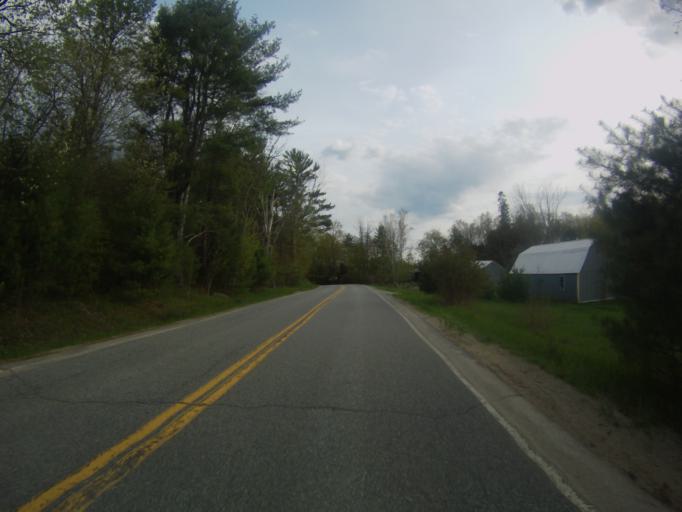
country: US
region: New York
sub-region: Warren County
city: Warrensburg
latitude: 43.7847
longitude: -73.9355
